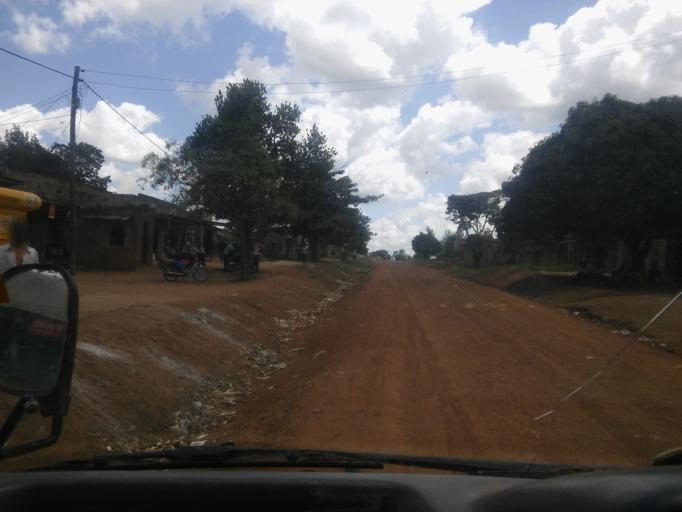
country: UG
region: Eastern Region
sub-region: Budaka District
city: Budaka
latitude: 1.0928
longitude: 34.0331
